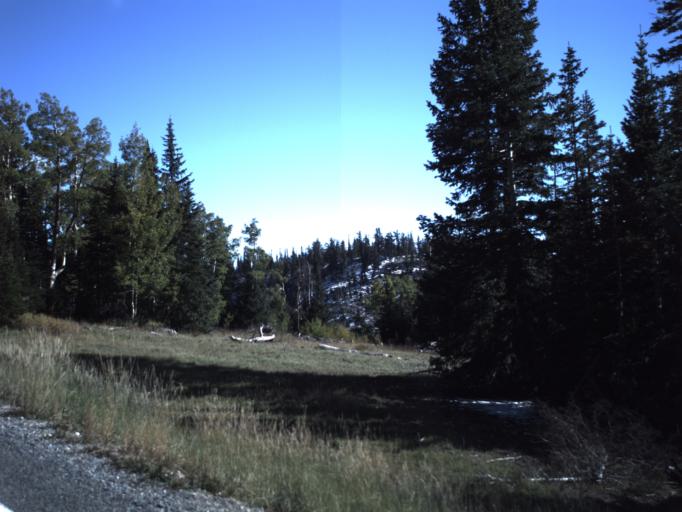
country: US
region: Utah
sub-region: Iron County
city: Parowan
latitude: 37.6775
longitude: -112.8467
